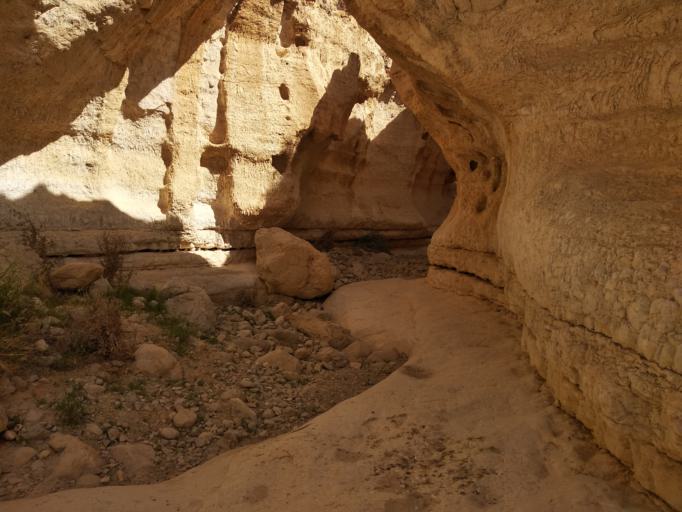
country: JO
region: Karak
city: Safi
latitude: 31.0100
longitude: 35.2888
